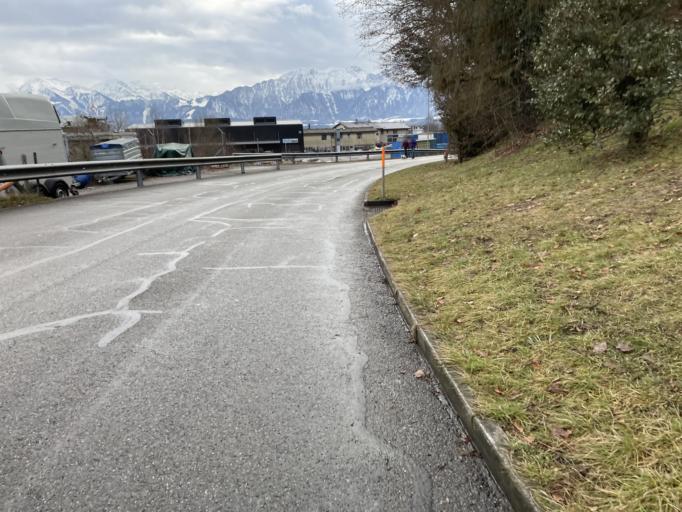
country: CH
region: Bern
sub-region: Thun District
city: Heimberg
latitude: 46.8004
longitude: 7.6029
